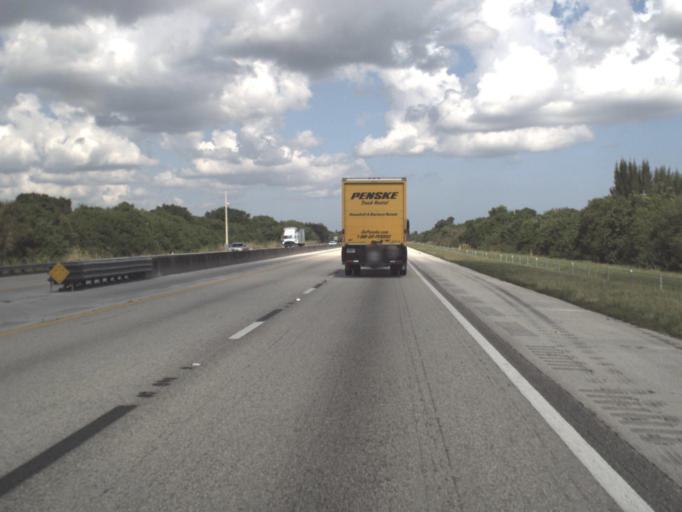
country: US
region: Florida
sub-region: Palm Beach County
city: Palm Beach Gardens
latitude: 26.8157
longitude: -80.1308
